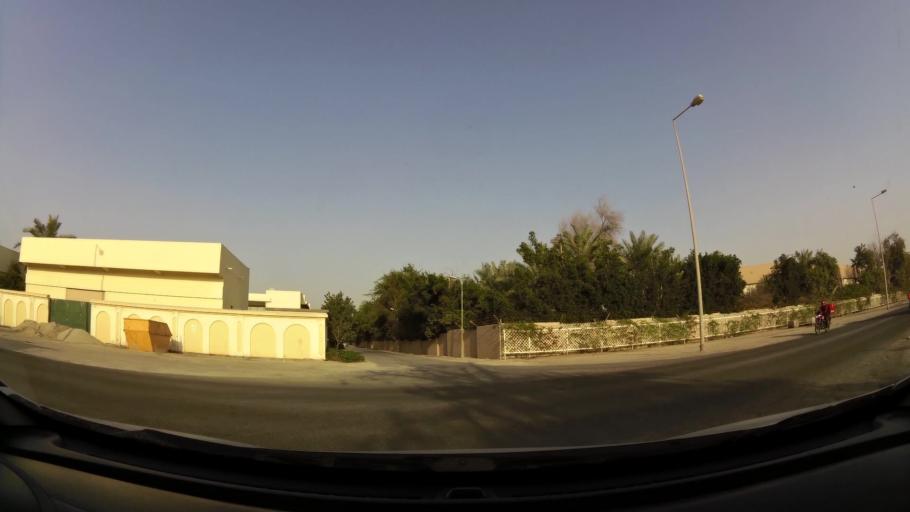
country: BH
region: Manama
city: Jidd Hafs
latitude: 26.2044
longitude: 50.4835
